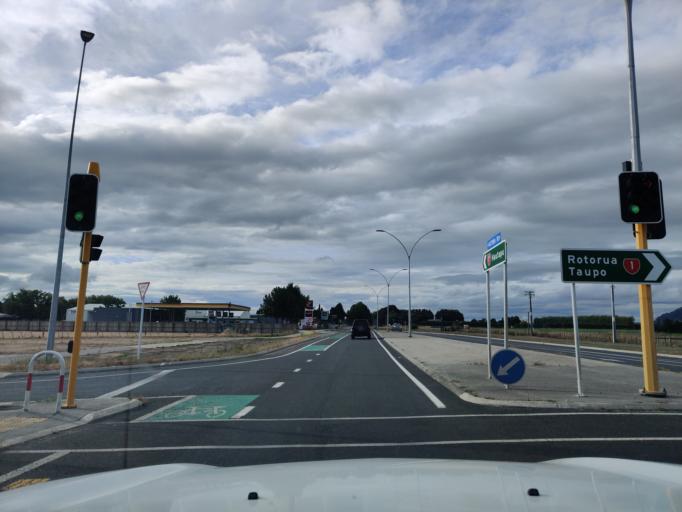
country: NZ
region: Waikato
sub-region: Waipa District
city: Cambridge
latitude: -37.8681
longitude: 175.4578
